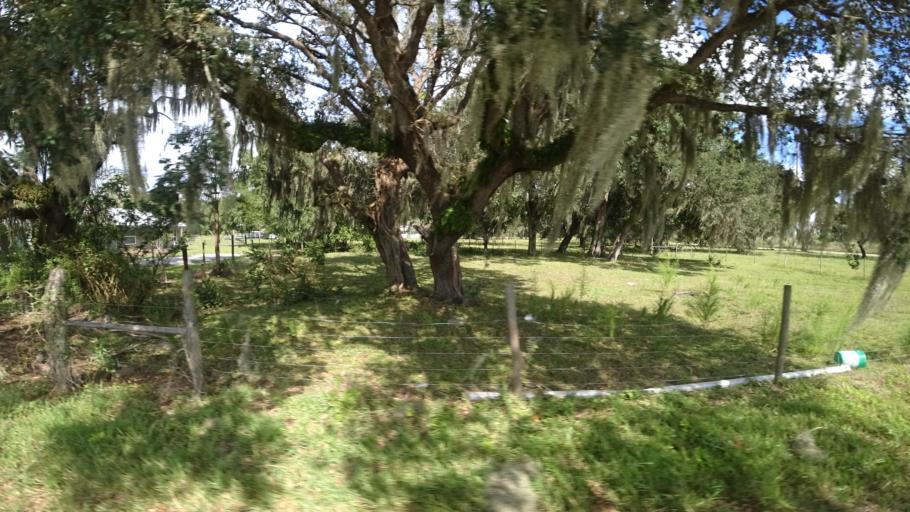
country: US
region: Florida
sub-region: Hardee County
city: Wauchula
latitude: 27.4685
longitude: -82.0759
